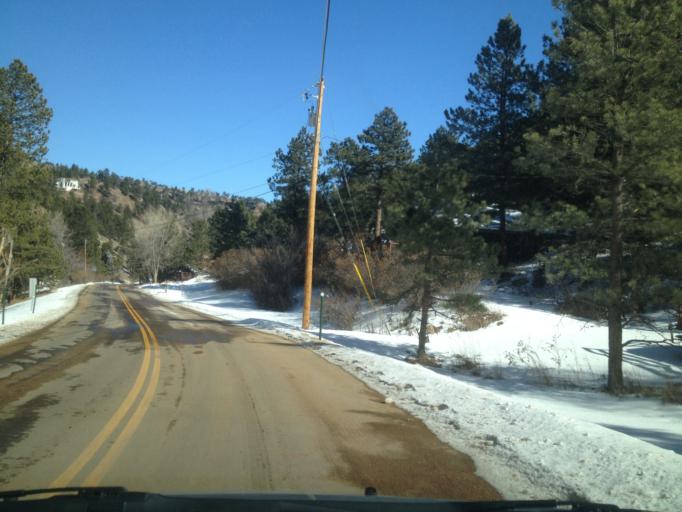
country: US
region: Colorado
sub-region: Boulder County
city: Boulder
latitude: 40.0611
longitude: -105.3150
